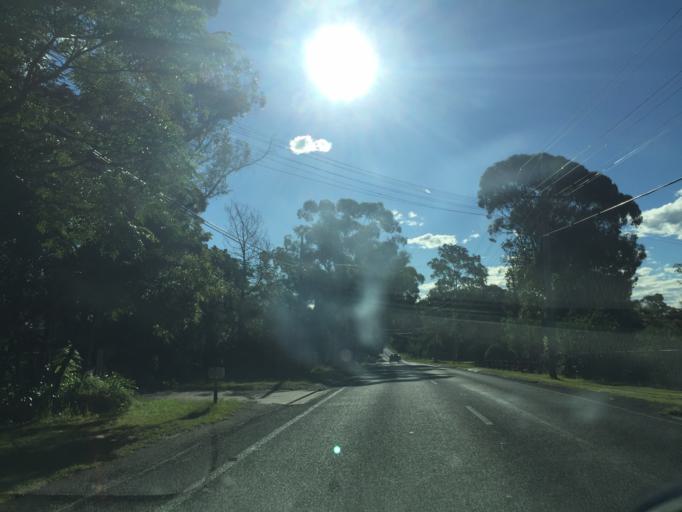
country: AU
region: New South Wales
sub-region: The Hills Shire
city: Glenhaven
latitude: -33.6956
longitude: 150.9844
